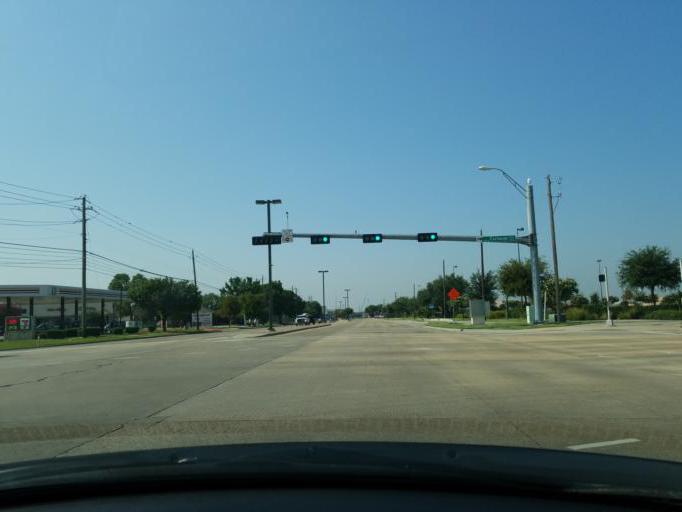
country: US
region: Texas
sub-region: Collin County
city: Allen
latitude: 33.1153
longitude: -96.6527
